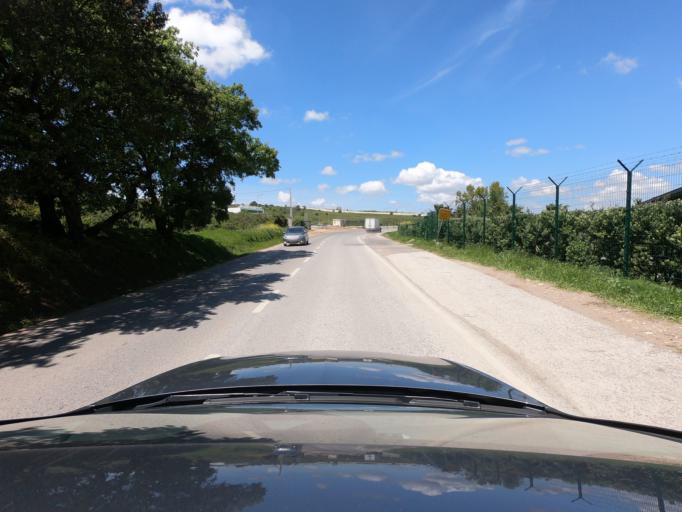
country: PT
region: Lisbon
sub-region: Amadora
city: Amadora
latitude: 38.7389
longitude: -9.2324
